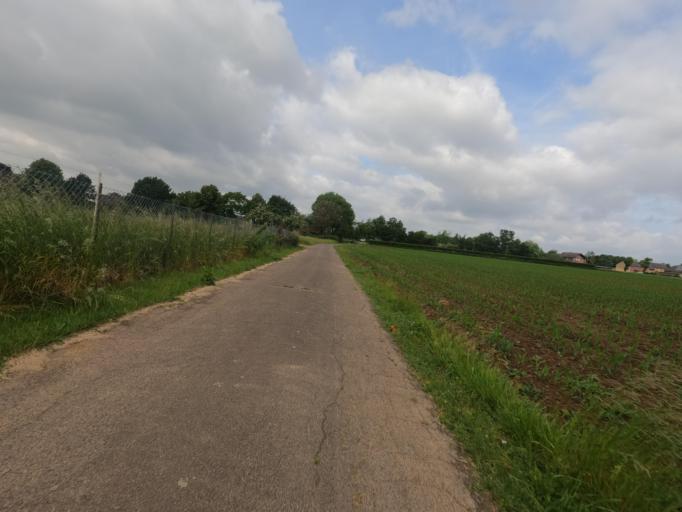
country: DE
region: North Rhine-Westphalia
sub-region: Regierungsbezirk Koln
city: Heinsberg
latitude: 51.0948
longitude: 6.1075
